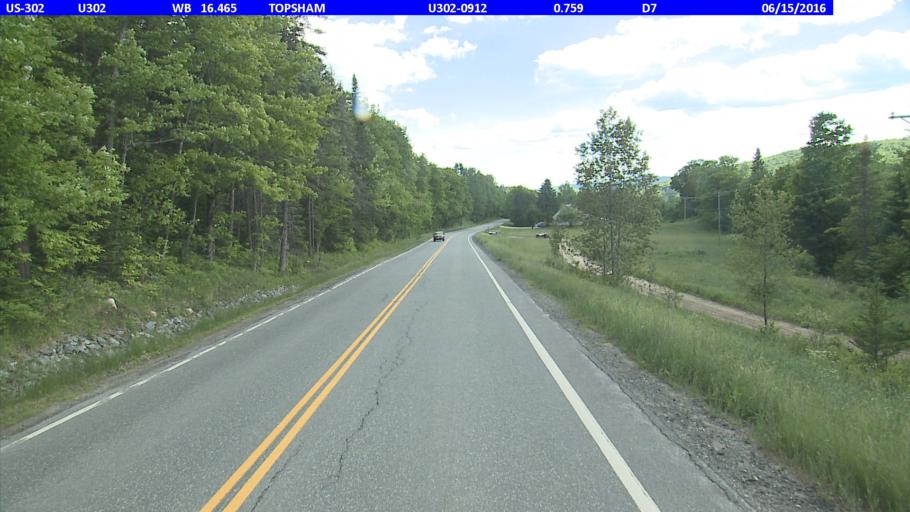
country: US
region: Vermont
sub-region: Washington County
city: South Barre
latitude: 44.1484
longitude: -72.3107
